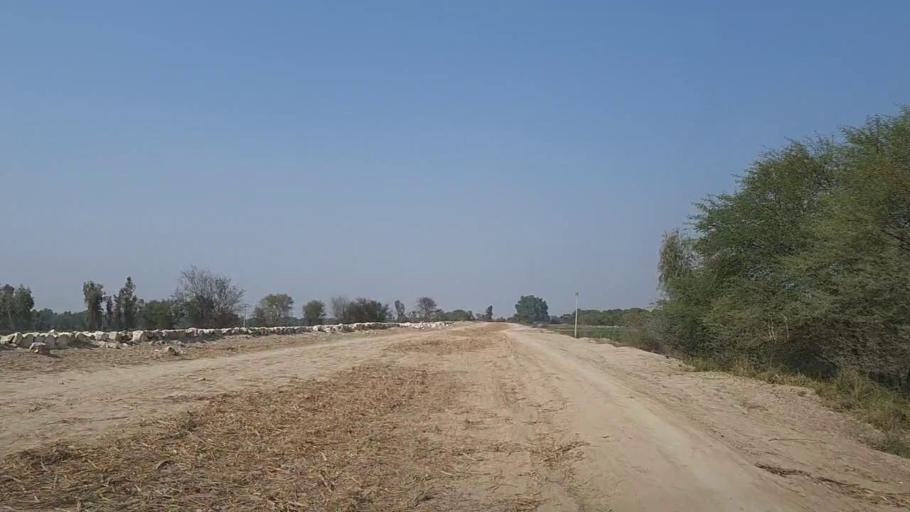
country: PK
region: Sindh
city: Moro
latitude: 26.8170
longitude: 67.9543
